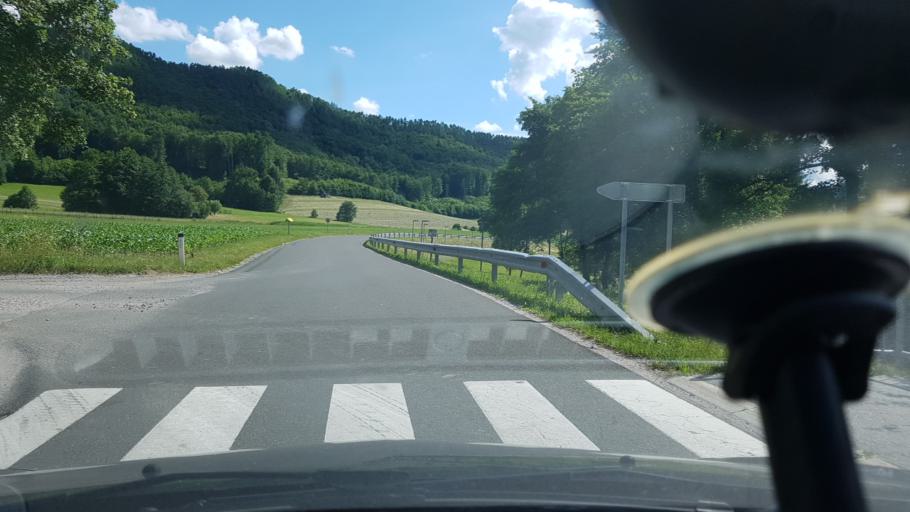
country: SI
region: Rogatec
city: Rogatec
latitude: 46.2402
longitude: 15.7130
